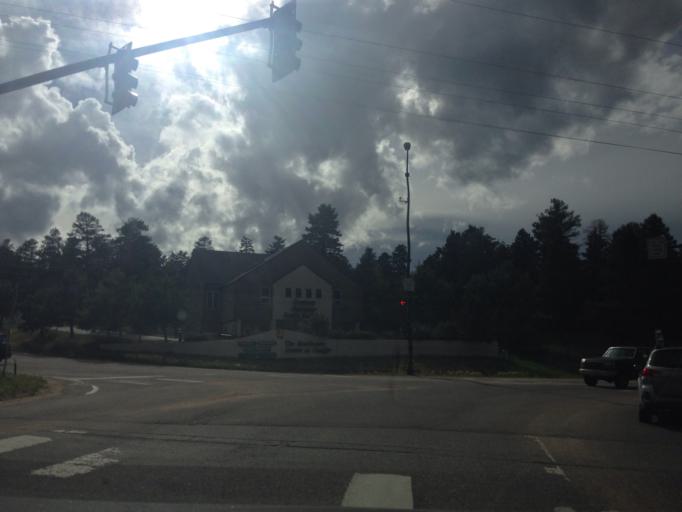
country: US
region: Colorado
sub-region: Jefferson County
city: Evergreen
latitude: 39.5201
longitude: -105.3065
